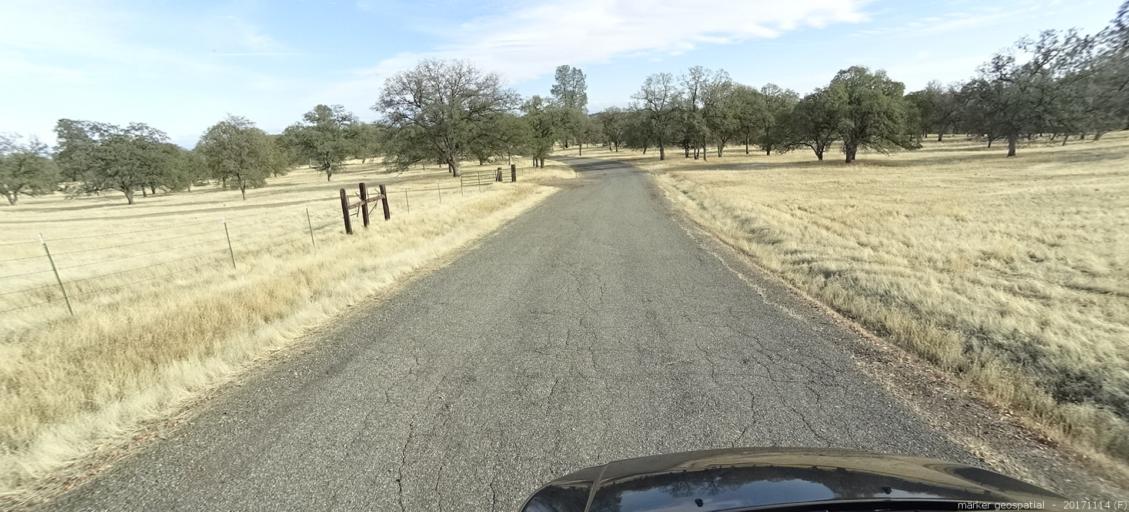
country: US
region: California
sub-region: Shasta County
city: Shasta
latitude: 40.3823
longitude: -122.5730
